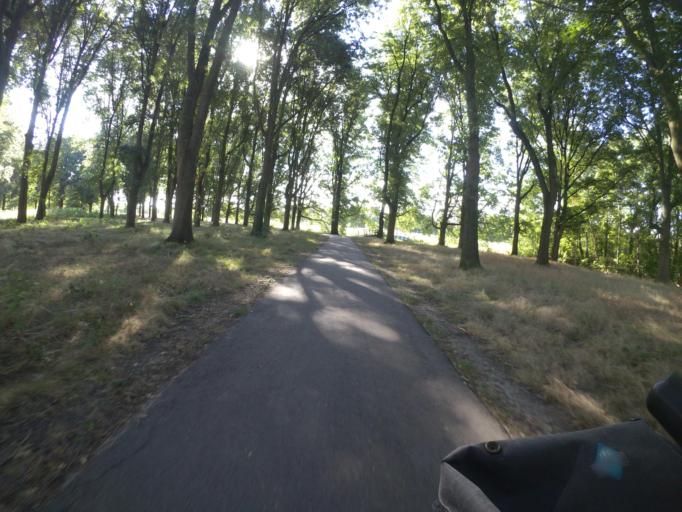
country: NL
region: Drenthe
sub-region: Gemeente Hoogeveen
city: Hoogeveen
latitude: 52.7112
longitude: 6.4858
